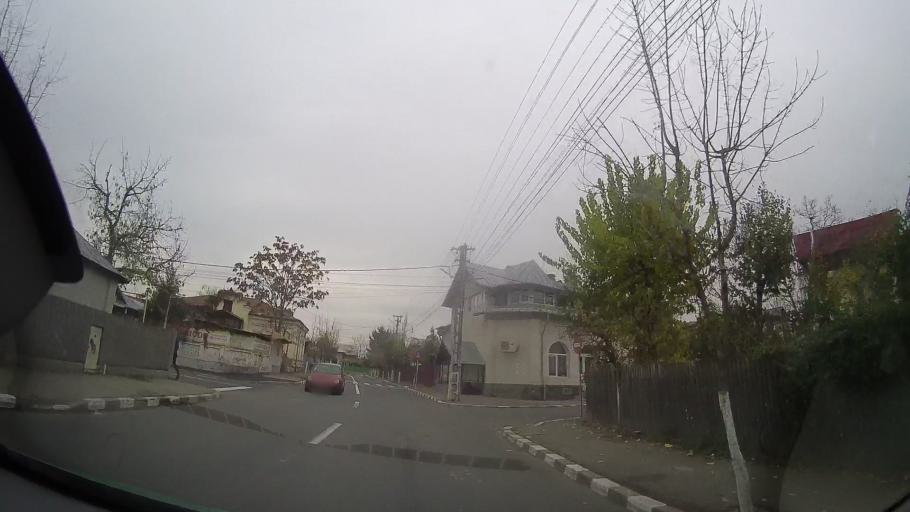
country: RO
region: Prahova
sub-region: Oras Urlati
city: Urlati
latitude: 44.9919
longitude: 26.2315
